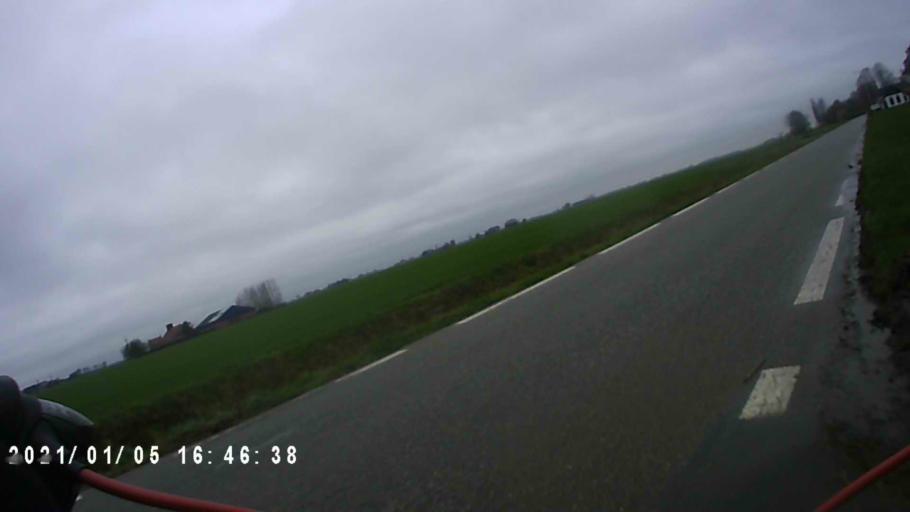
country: NL
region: Groningen
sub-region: Gemeente  Oldambt
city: Winschoten
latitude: 53.2235
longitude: 7.0529
